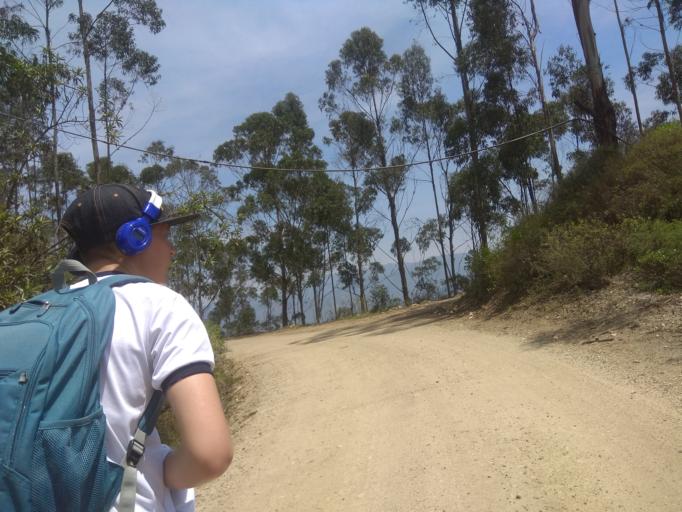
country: CO
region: Boyaca
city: Socha Viejo
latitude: 5.9814
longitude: -72.7320
